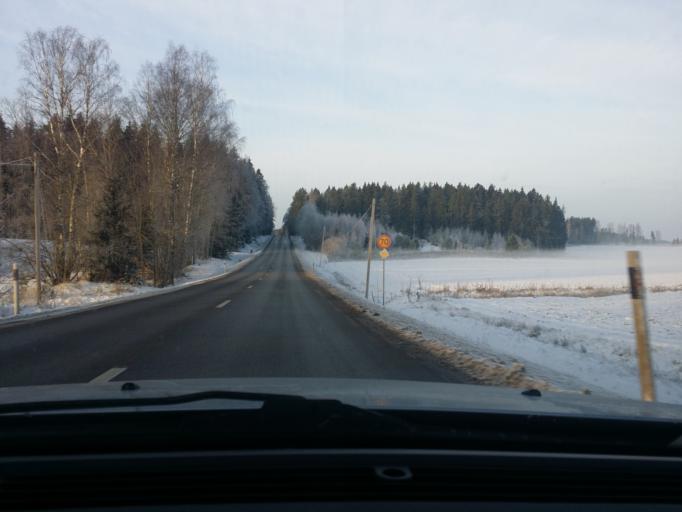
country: SE
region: OErebro
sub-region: Lindesbergs Kommun
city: Frovi
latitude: 59.5165
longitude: 15.3374
